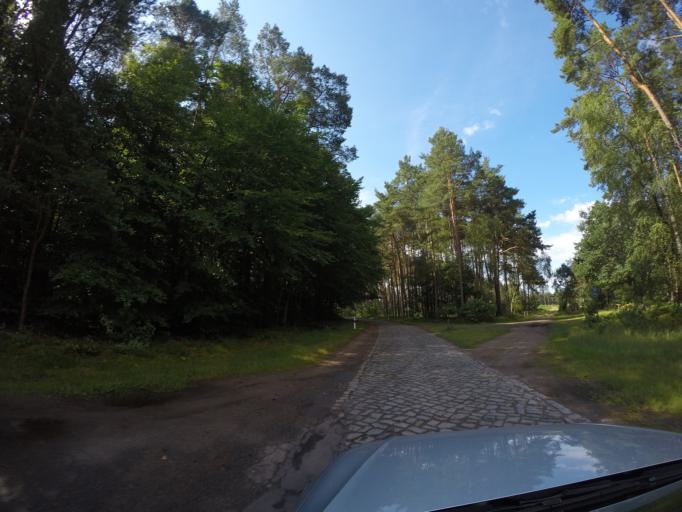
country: DE
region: Mecklenburg-Vorpommern
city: Wesenberg
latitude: 53.2843
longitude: 12.8861
